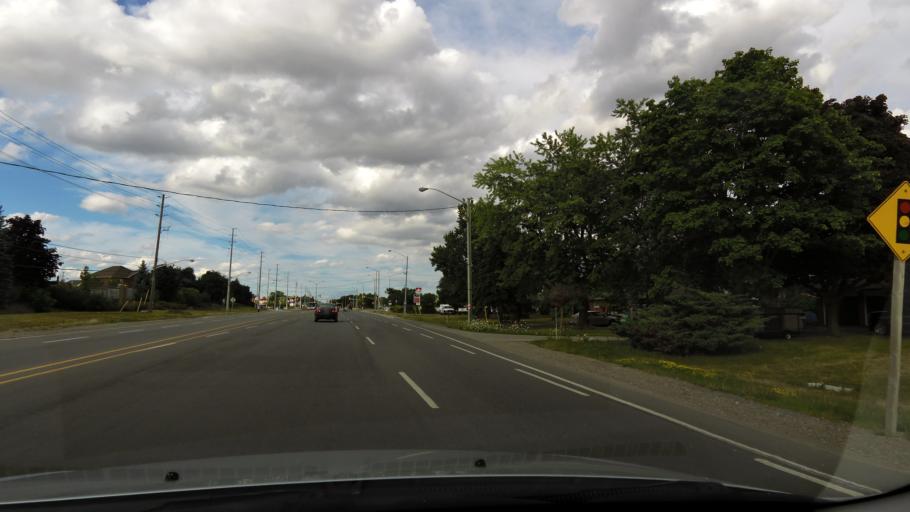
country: CA
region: Ontario
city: Brampton
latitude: 43.7321
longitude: -79.8268
